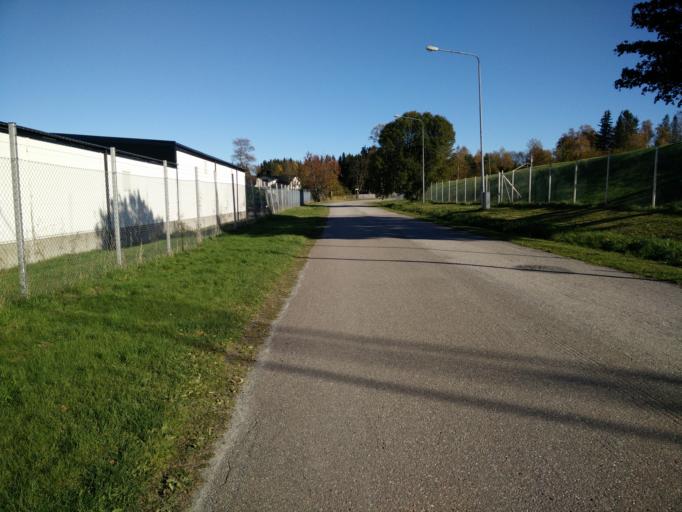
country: SE
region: Vaesternorrland
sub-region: Haernoesands Kommun
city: Haernoesand
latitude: 62.6390
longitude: 17.9664
